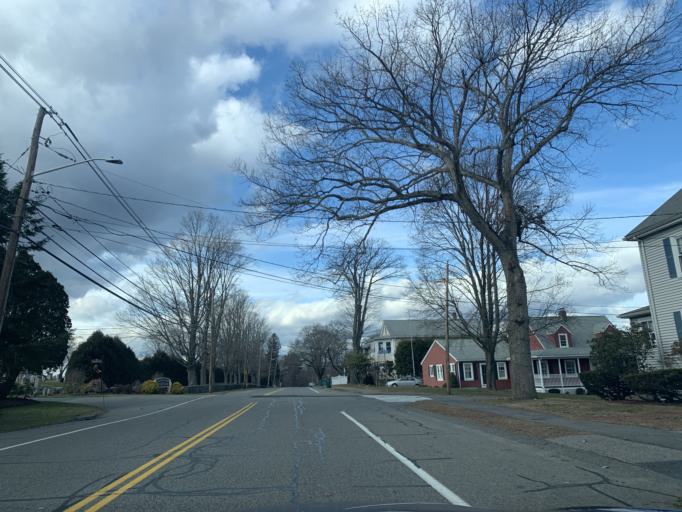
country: US
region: Massachusetts
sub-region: Norfolk County
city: Norwood
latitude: 42.1956
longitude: -71.2143
